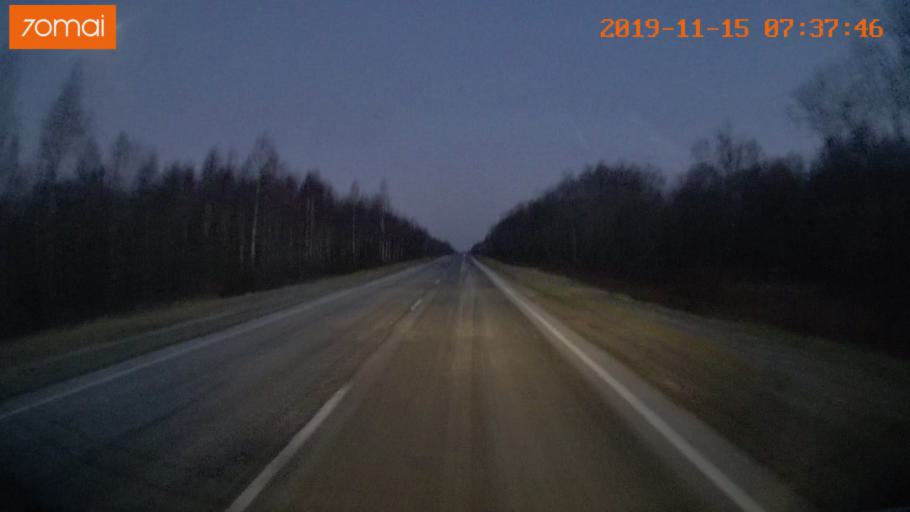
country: RU
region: Vologda
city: Sheksna
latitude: 58.7499
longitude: 38.4148
